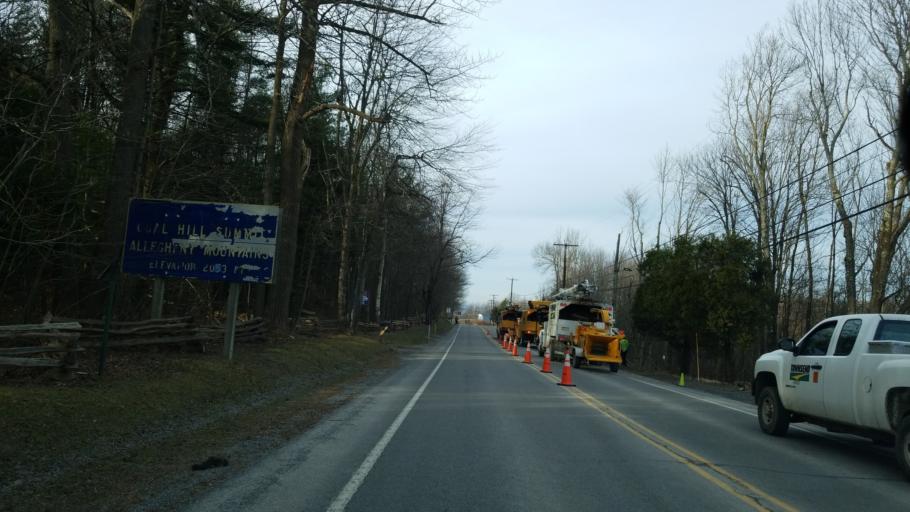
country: US
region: Pennsylvania
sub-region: Clearfield County
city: Sandy
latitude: 41.0470
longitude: -78.7029
